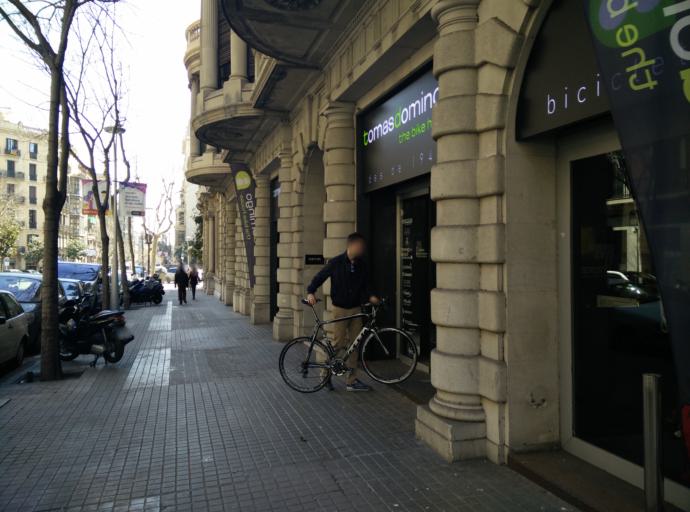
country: ES
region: Catalonia
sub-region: Provincia de Barcelona
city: Eixample
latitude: 41.3964
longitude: 2.1644
